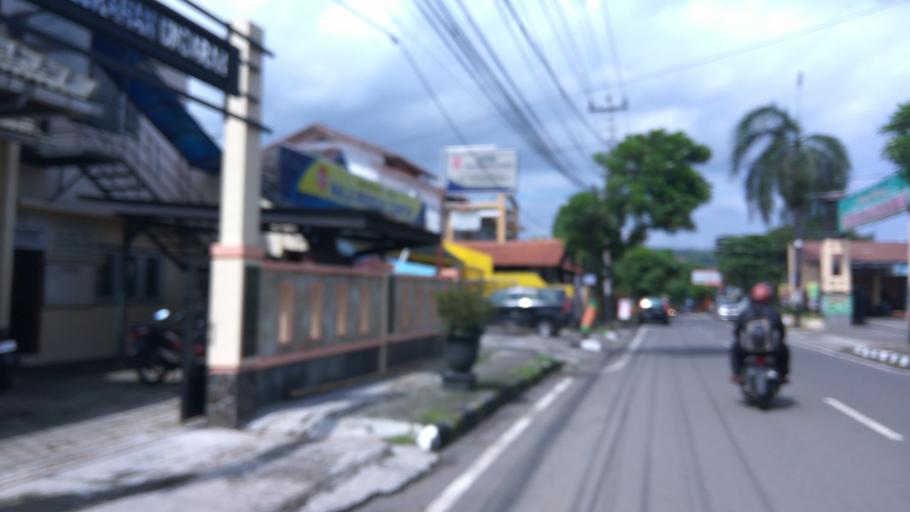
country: ID
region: Central Java
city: Ungaran
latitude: -7.1288
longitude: 110.4088
